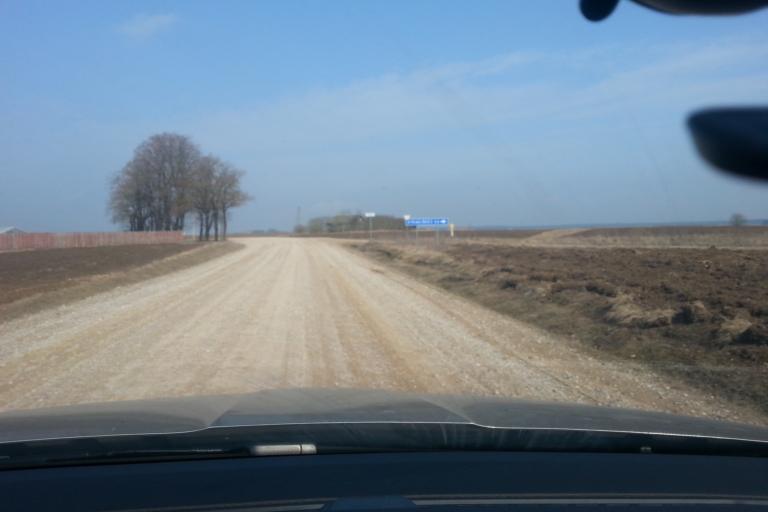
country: LT
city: Trakai
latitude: 54.5846
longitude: 24.9771
